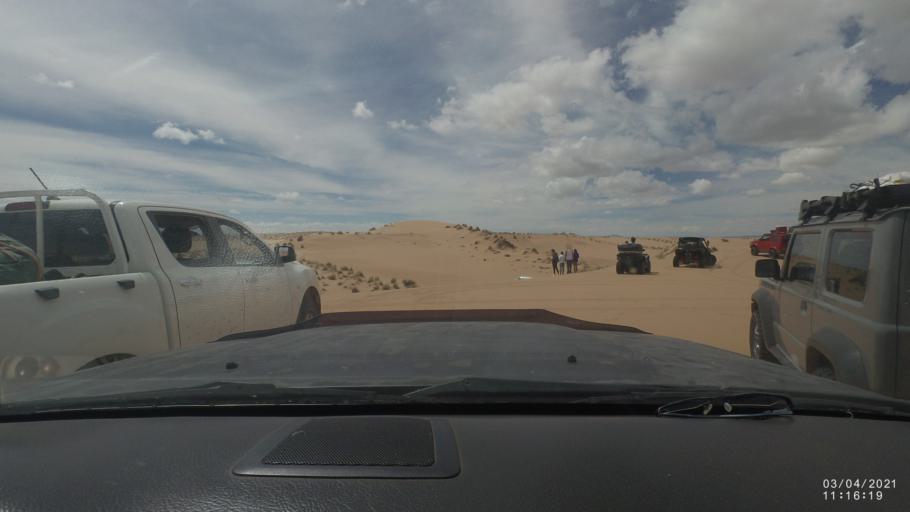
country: BO
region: Oruro
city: Poopo
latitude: -18.7049
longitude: -67.5145
